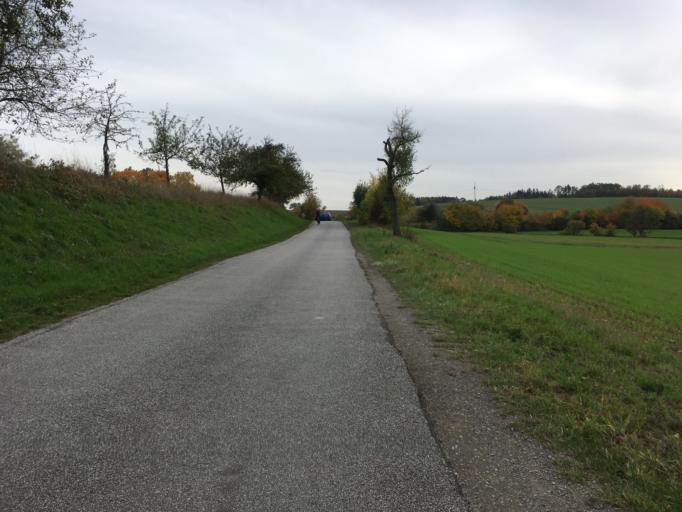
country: DE
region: Baden-Wuerttemberg
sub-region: Karlsruhe Region
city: Buchen
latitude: 49.5085
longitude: 9.3289
